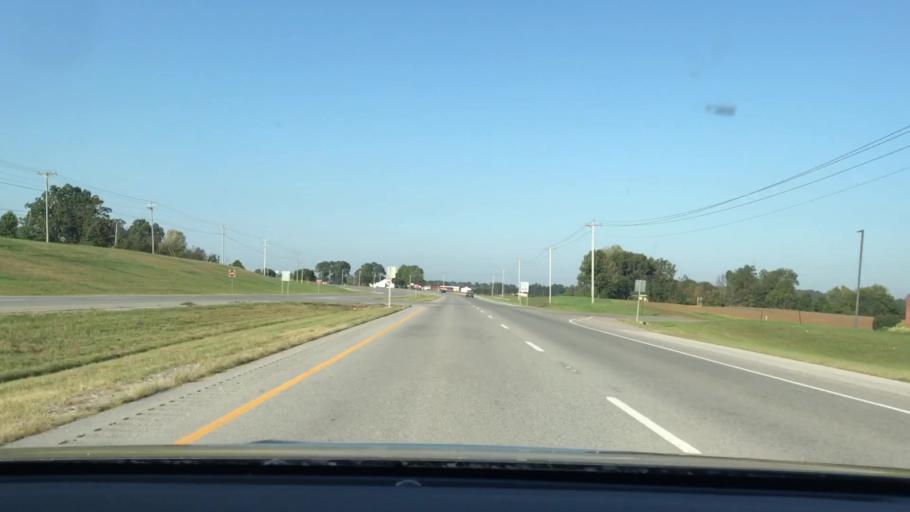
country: US
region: Kentucky
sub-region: Trigg County
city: Cadiz
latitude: 36.8768
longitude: -87.7469
